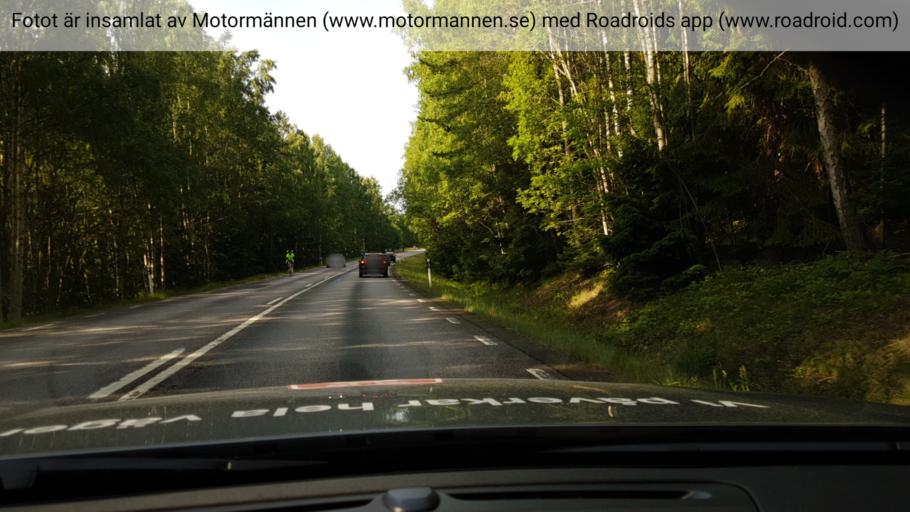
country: SE
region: OErebro
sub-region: Askersunds Kommun
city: Askersund
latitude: 58.7229
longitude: 14.7592
